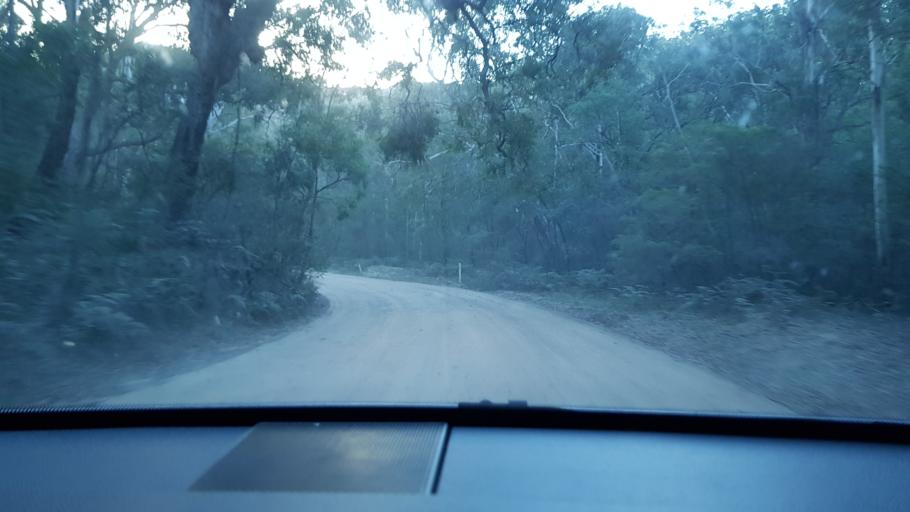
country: AU
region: New South Wales
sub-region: Lithgow
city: Portland
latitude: -33.1843
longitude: 150.2415
